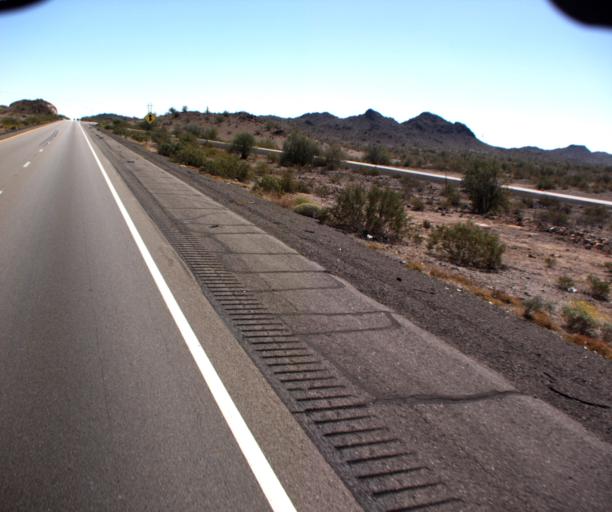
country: US
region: Arizona
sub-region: La Paz County
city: Salome
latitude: 33.6125
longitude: -113.6449
